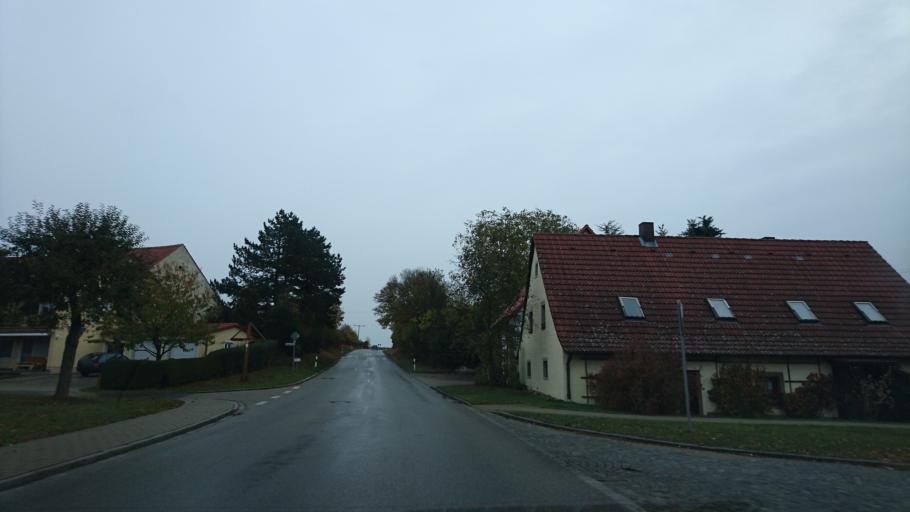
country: DE
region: Bavaria
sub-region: Regierungsbezirk Mittelfranken
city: Hottingen
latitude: 49.0747
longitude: 11.0242
